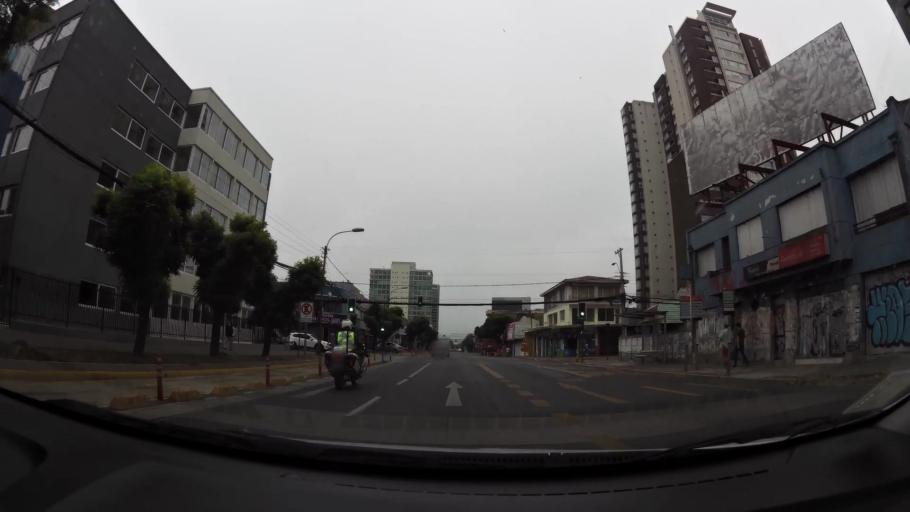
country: CL
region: Biobio
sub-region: Provincia de Concepcion
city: Concepcion
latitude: -36.8298
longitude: -73.0552
